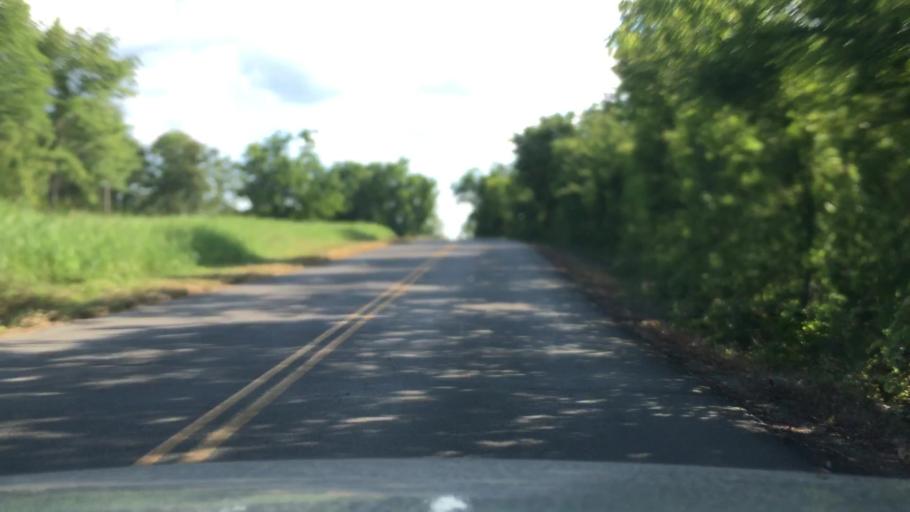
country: US
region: Oklahoma
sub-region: Muskogee County
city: Fort Gibson
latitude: 35.9143
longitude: -95.1579
